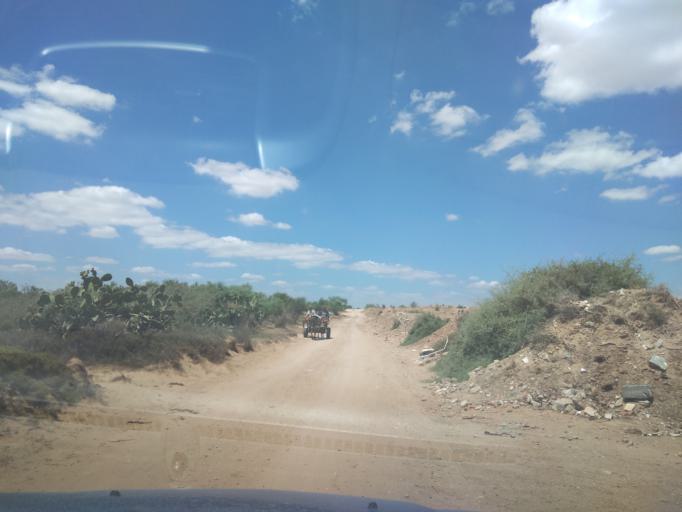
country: TN
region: Susah
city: Harqalah
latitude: 36.1648
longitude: 10.4485
